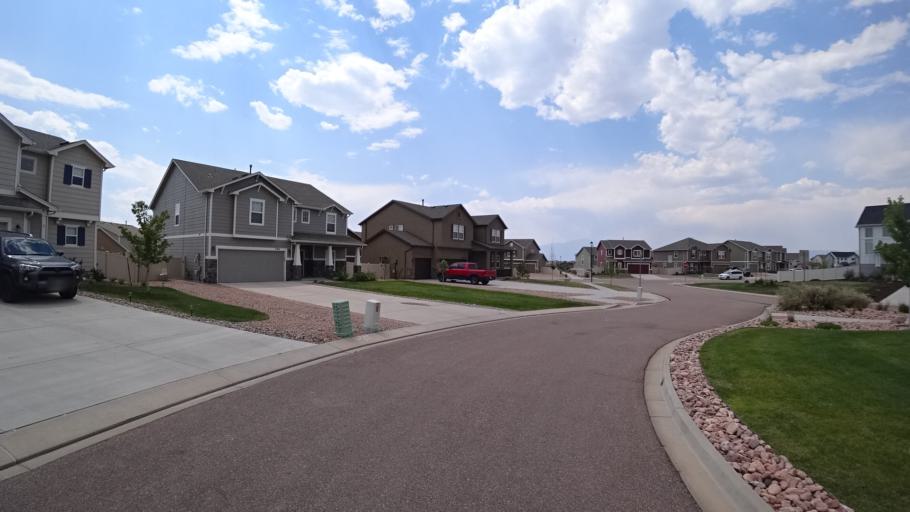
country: US
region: Colorado
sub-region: El Paso County
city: Black Forest
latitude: 38.9536
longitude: -104.6919
